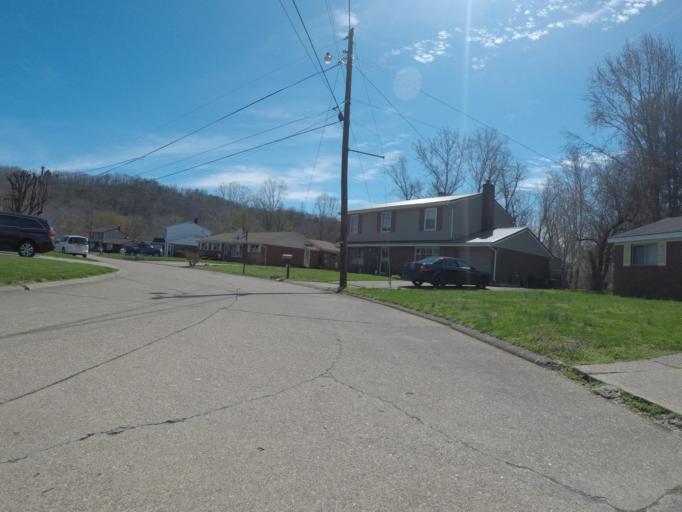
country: US
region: West Virginia
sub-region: Cabell County
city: Pea Ridge
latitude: 38.3976
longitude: -82.3175
